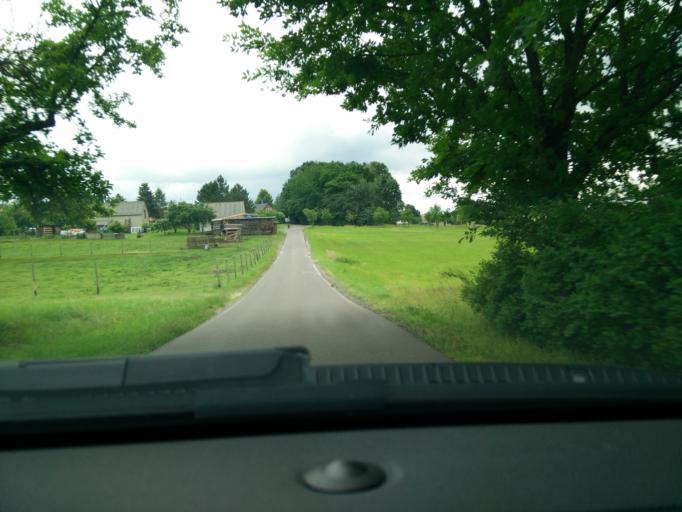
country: DE
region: Saxony
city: Geithain
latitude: 51.0864
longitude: 12.6515
